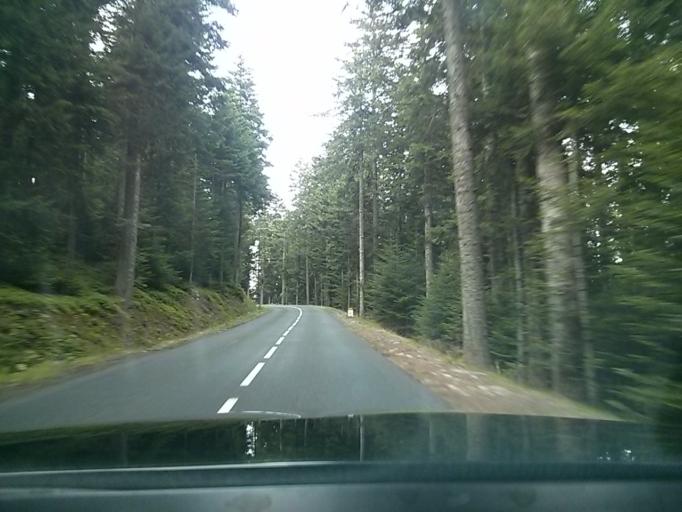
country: FR
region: Rhone-Alpes
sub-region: Departement de la Loire
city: Saint-Genest-Malifaux
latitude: 45.3567
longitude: 4.4777
